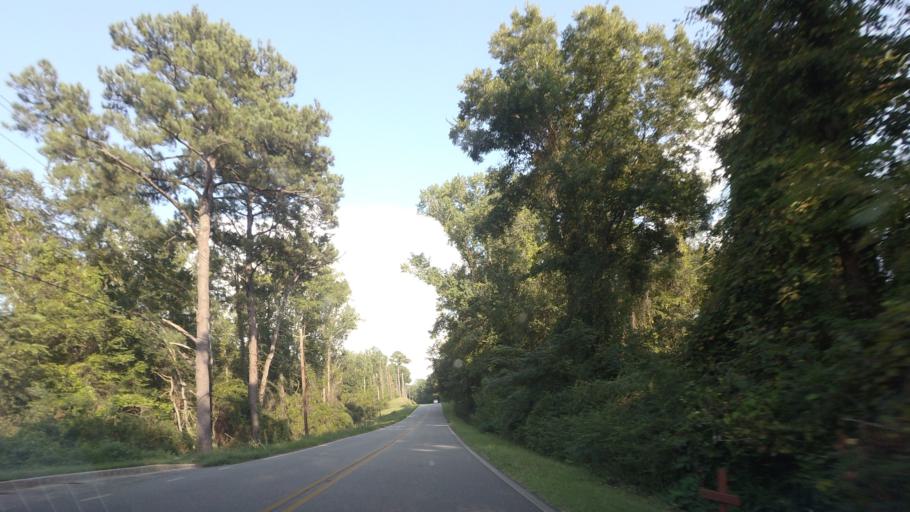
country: US
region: Georgia
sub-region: Bibb County
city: Macon
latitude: 32.8483
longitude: -83.7062
